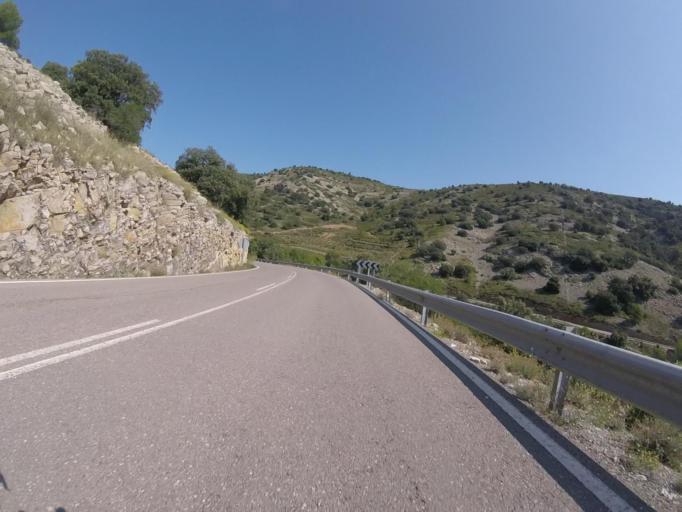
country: ES
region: Valencia
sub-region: Provincia de Castello
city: Benafigos
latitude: 40.2669
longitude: -0.2333
